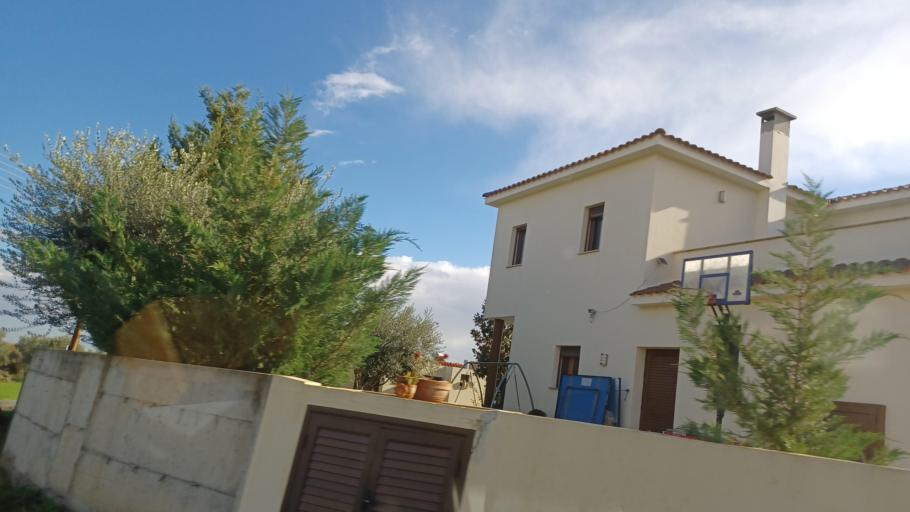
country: CY
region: Lefkosia
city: Lythrodontas
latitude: 34.9407
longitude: 33.2965
